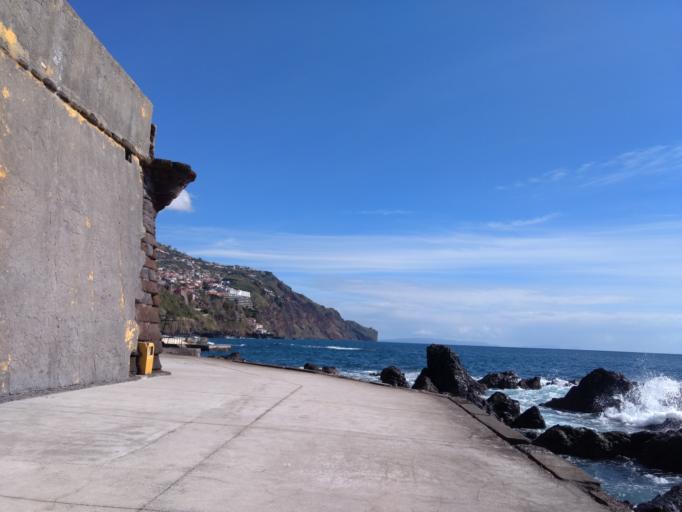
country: PT
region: Madeira
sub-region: Funchal
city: Funchal
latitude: 32.6464
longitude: -16.8987
